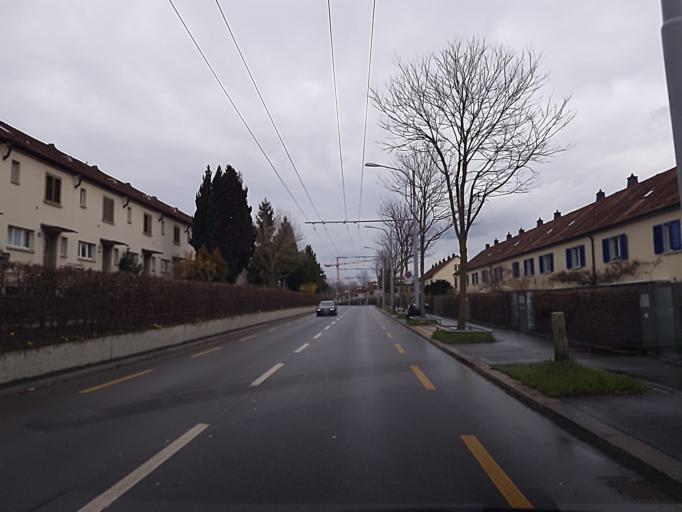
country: CH
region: Zurich
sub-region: Bezirk Zuerich
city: Zuerich (Kreis 3) / Alt-Wiedikon
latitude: 47.3552
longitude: 8.5108
